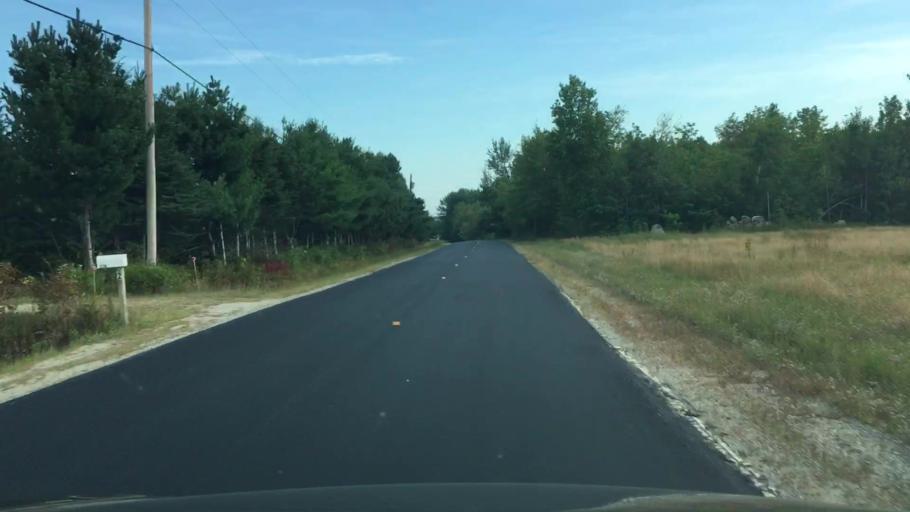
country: US
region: Maine
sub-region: Hancock County
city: Orland
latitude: 44.5533
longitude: -68.6213
